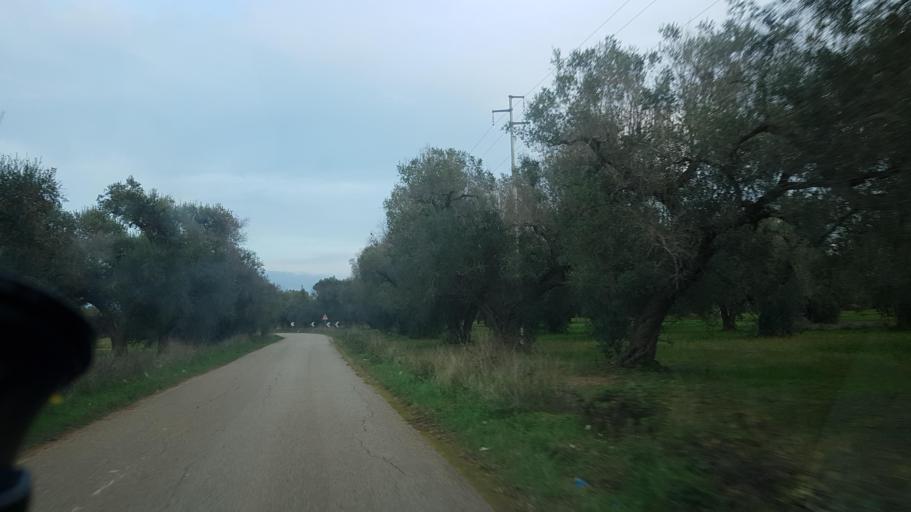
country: IT
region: Apulia
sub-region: Provincia di Brindisi
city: Mesagne
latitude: 40.5365
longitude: 17.7656
